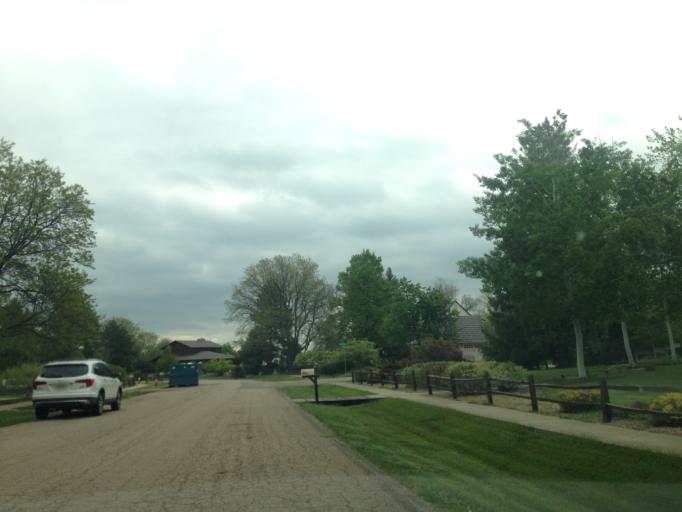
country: US
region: Colorado
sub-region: Boulder County
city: Louisville
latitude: 40.0048
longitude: -105.1708
